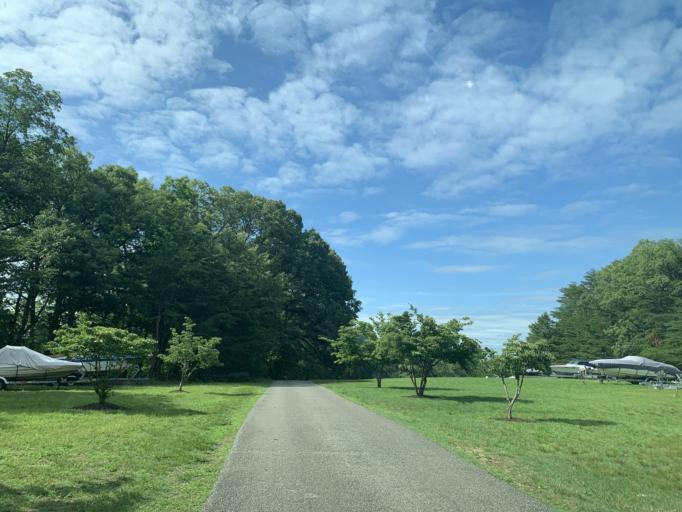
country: US
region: Maryland
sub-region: Anne Arundel County
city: Arden on the Severn
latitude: 39.0770
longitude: -76.6110
